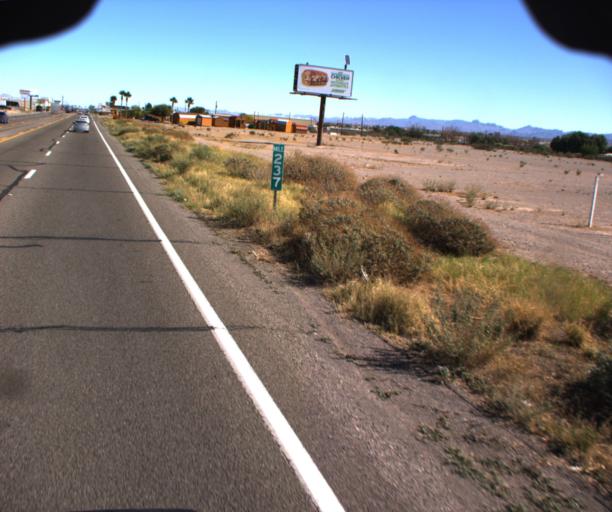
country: US
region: Arizona
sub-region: Mohave County
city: Mohave Valley
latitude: 35.0054
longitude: -114.5979
